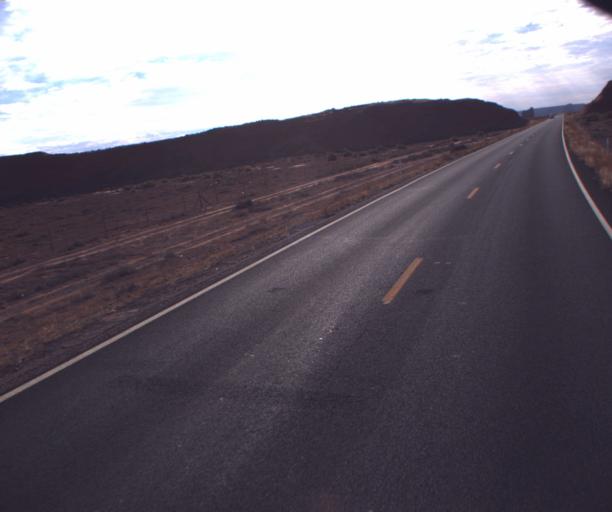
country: US
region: Arizona
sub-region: Apache County
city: Many Farms
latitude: 36.7648
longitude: -109.6527
